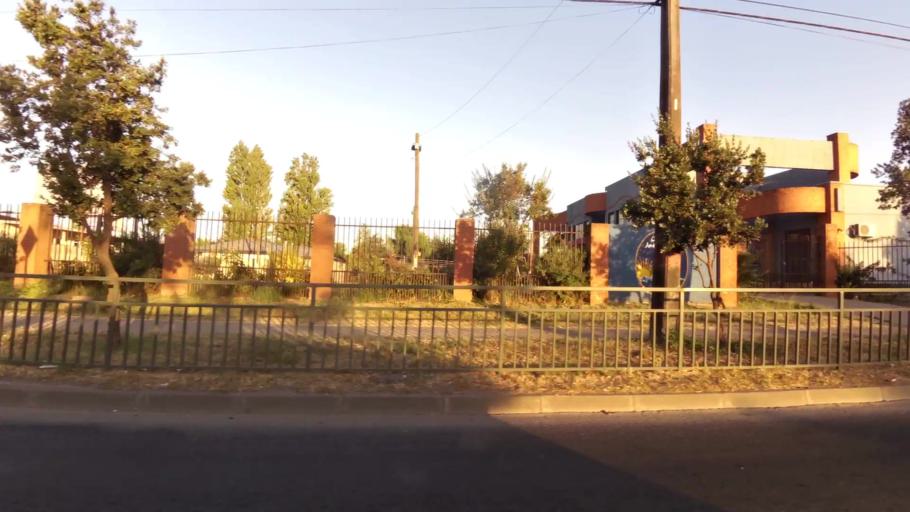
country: CL
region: Maule
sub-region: Provincia de Talca
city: Talca
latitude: -35.4480
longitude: -71.6492
